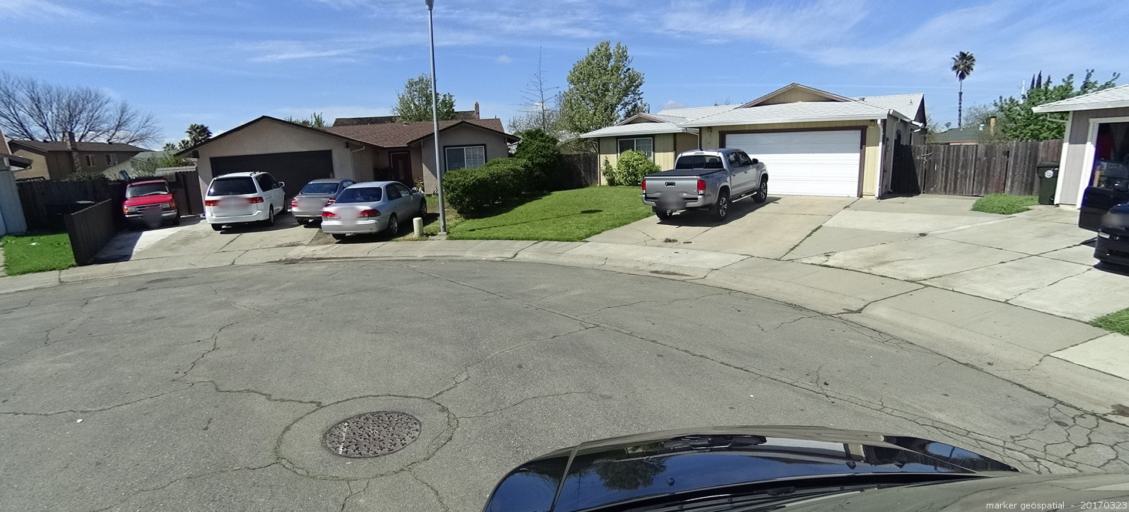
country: US
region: California
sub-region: Sacramento County
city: Florin
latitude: 38.5059
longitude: -121.4206
